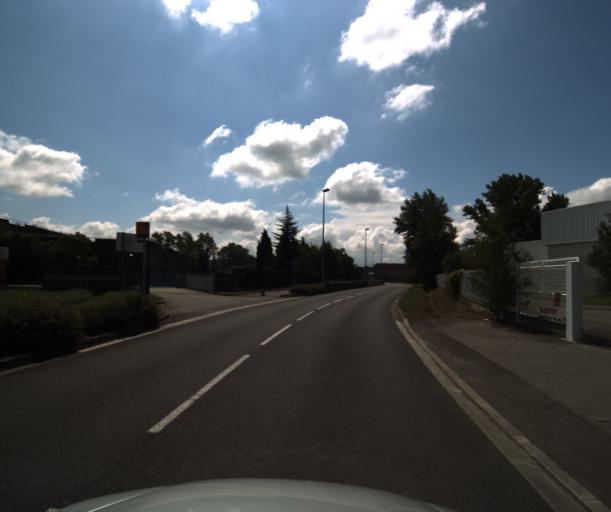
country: FR
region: Midi-Pyrenees
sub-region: Departement de la Haute-Garonne
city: Portet-sur-Garonne
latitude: 43.5340
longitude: 1.4102
